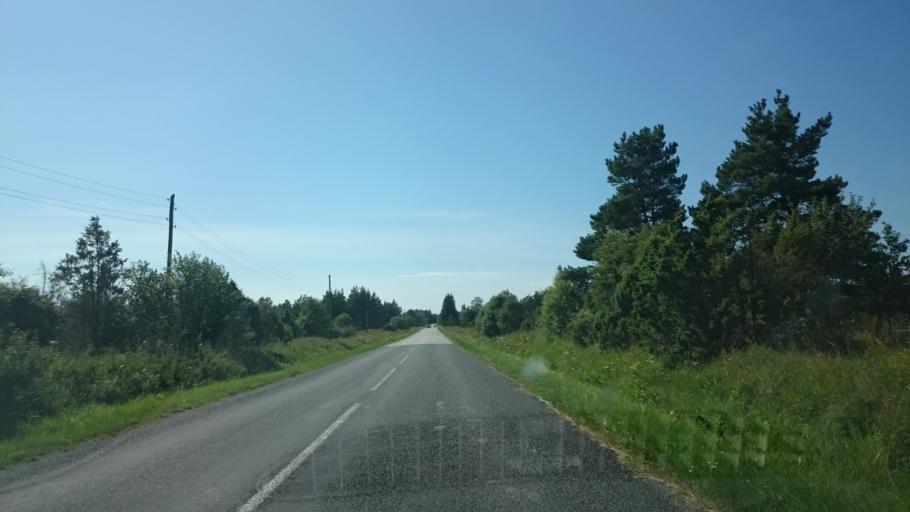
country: EE
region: Saare
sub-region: Orissaare vald
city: Orissaare
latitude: 58.5692
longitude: 22.7590
